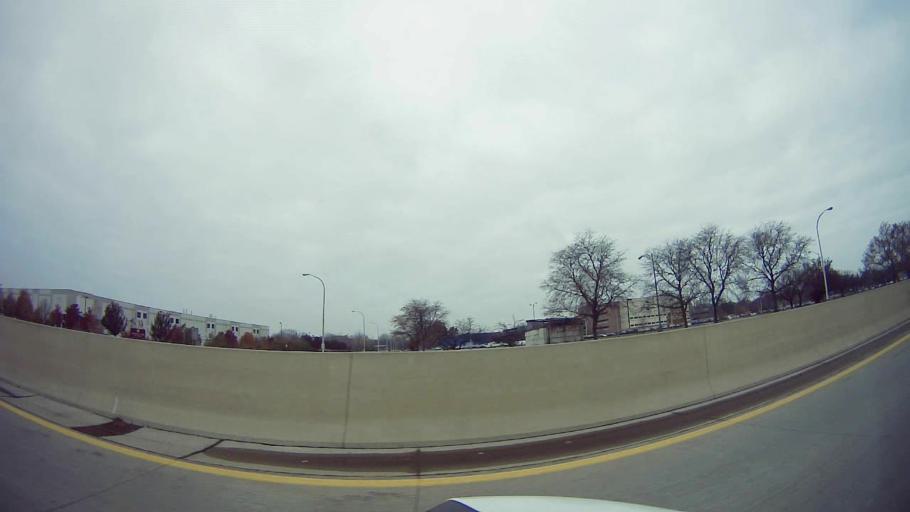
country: US
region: Michigan
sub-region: Oakland County
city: Southfield
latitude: 42.4628
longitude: -83.2205
